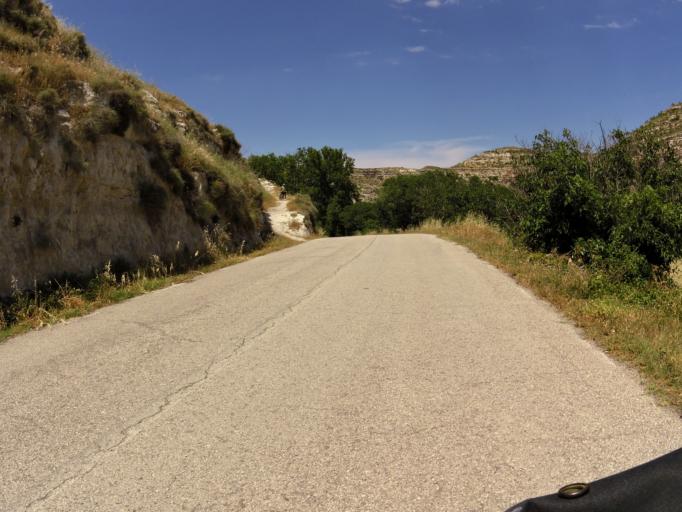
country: ES
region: Castille-La Mancha
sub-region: Provincia de Albacete
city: Jorquera
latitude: 39.1753
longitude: -1.5179
